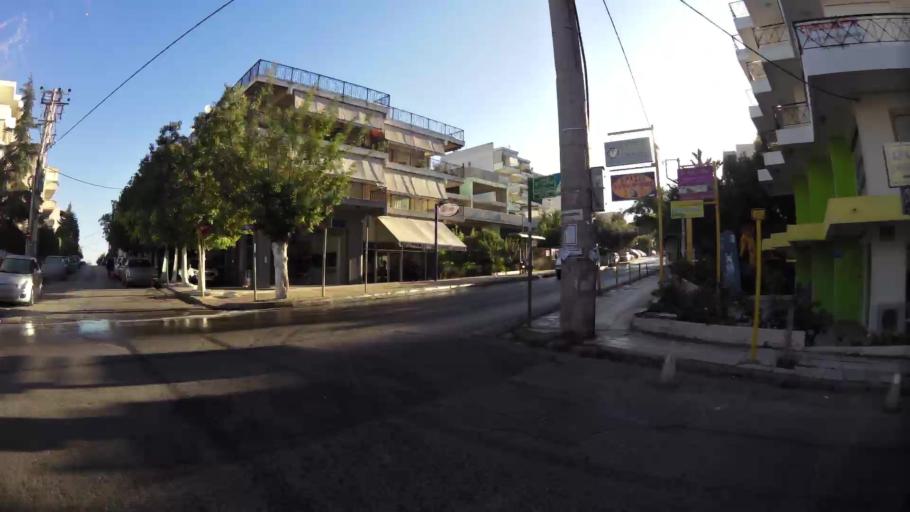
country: GR
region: Attica
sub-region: Nomarchia Athinas
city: Lykovrysi
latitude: 38.0634
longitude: 23.7791
